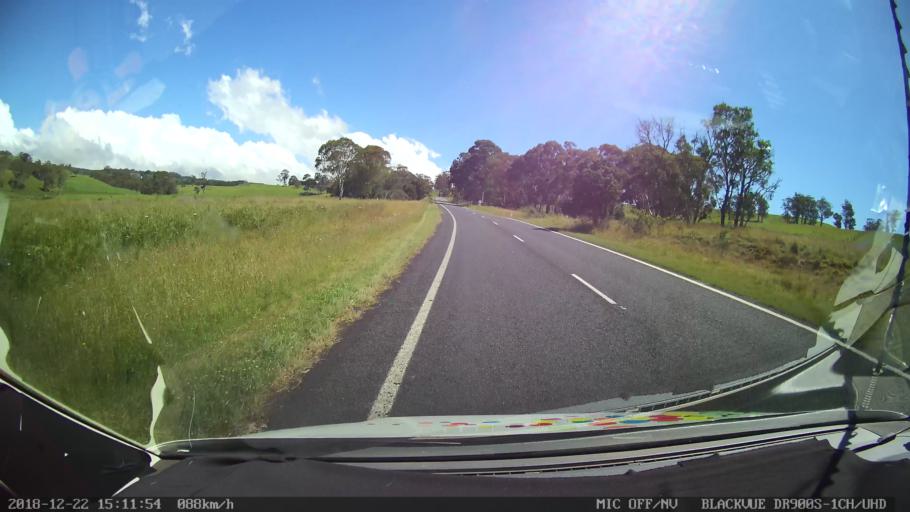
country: AU
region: New South Wales
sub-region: Bellingen
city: Dorrigo
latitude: -30.3491
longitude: 152.3981
